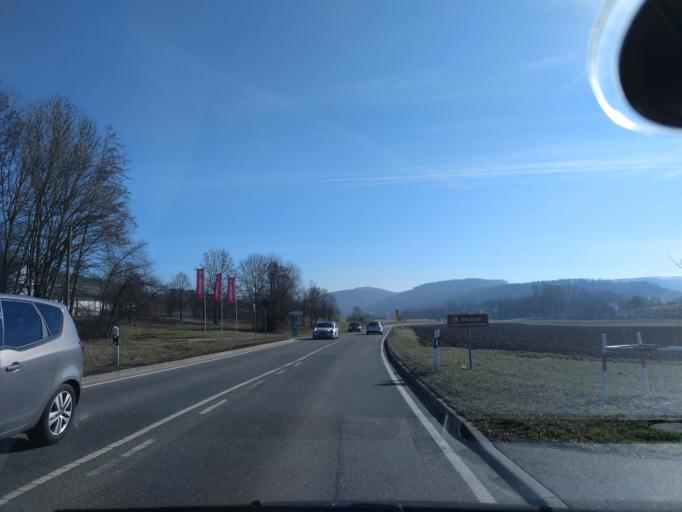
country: DE
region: Baden-Wuerttemberg
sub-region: Regierungsbezirk Stuttgart
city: Bretzfeld
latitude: 49.1612
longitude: 9.4569
